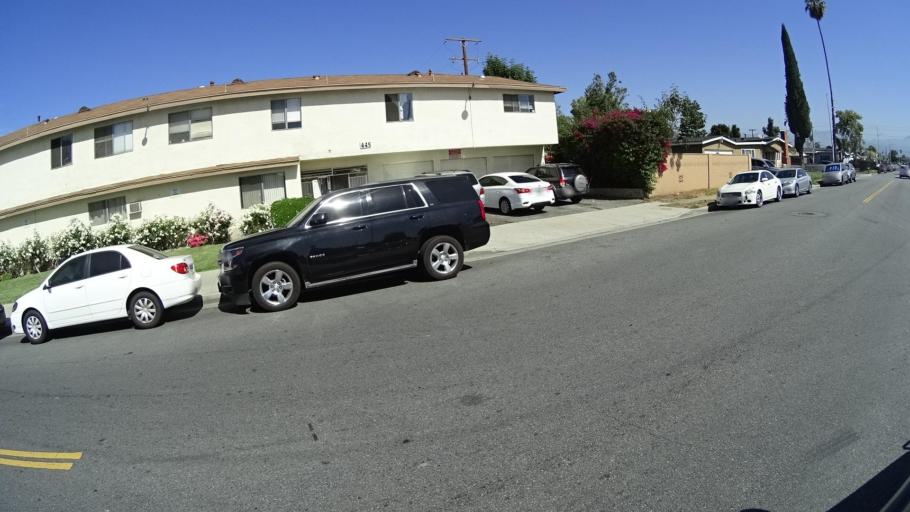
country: US
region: California
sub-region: Los Angeles County
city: West Puente Valley
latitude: 34.0426
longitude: -117.9744
